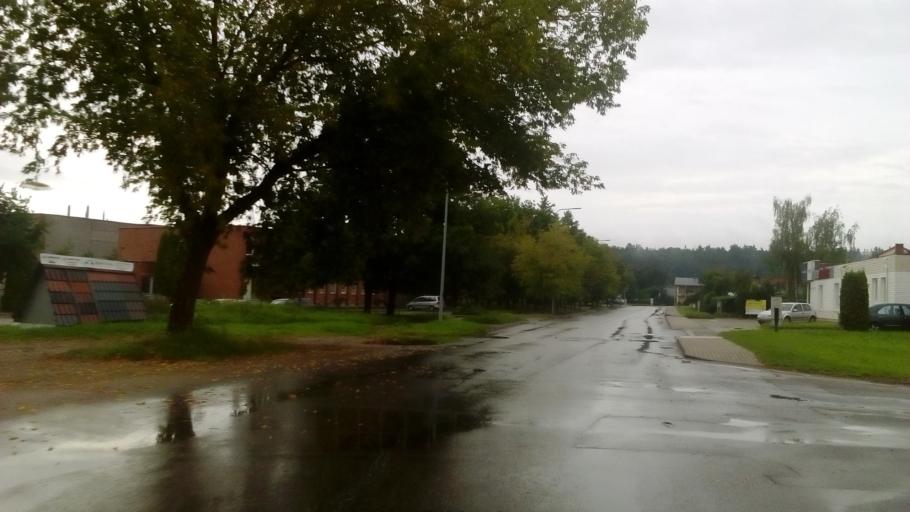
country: LT
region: Alytaus apskritis
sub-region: Alytus
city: Alytus
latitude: 54.3891
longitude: 24.0399
